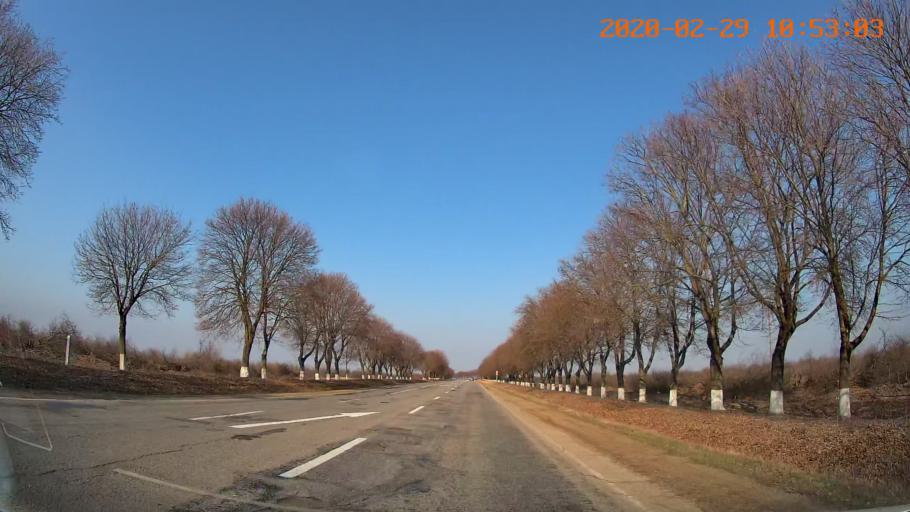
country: MD
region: Telenesti
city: Grigoriopol
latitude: 47.1117
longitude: 29.3416
